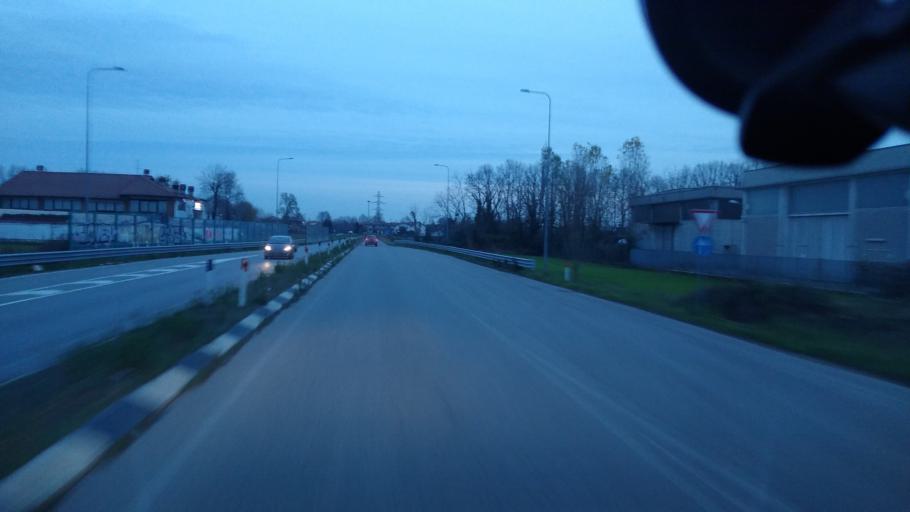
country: IT
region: Lombardy
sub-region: Provincia di Bergamo
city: Arcene
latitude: 45.5850
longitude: 9.6136
